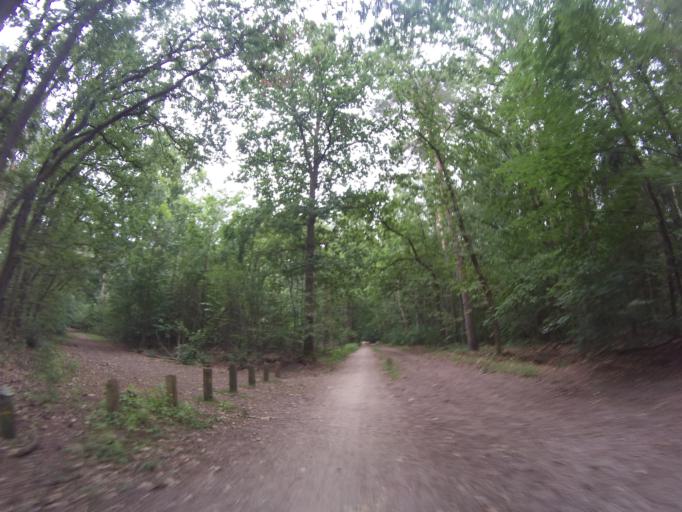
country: NL
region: North Holland
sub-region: Gemeente Bussum
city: Bussum
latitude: 52.2499
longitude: 5.1576
